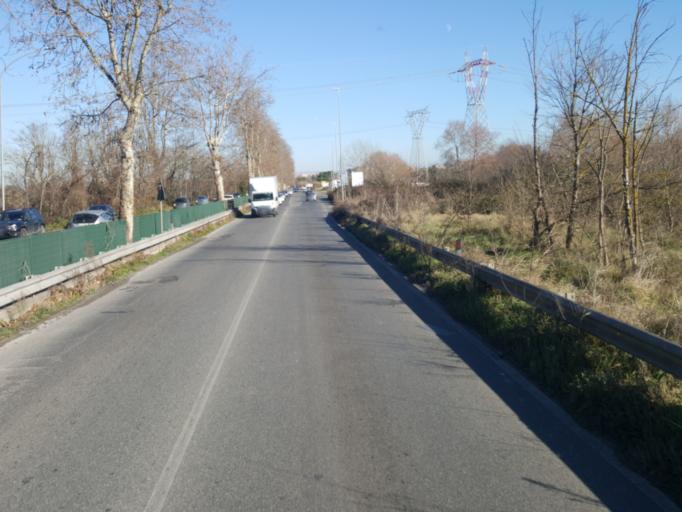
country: IT
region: Latium
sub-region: Citta metropolitana di Roma Capitale
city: Vitinia
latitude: 41.7928
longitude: 12.3901
